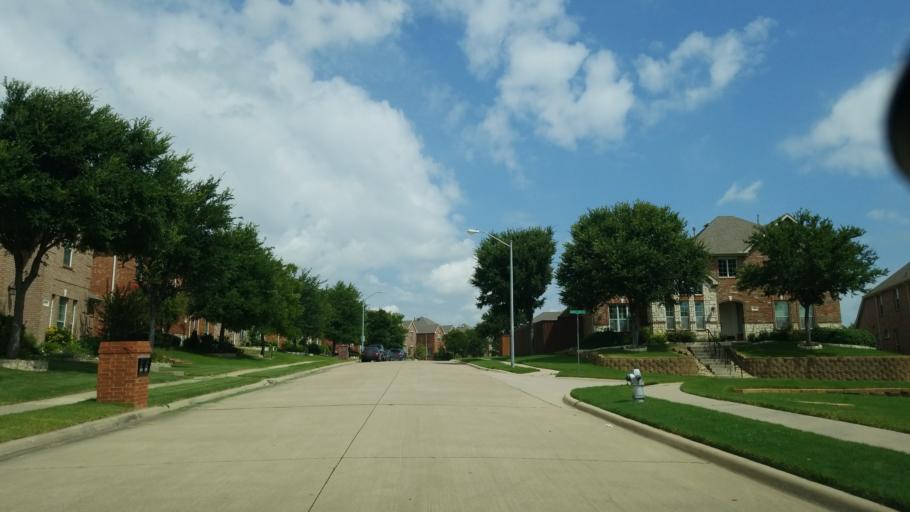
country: US
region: Texas
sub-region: Dallas County
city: Coppell
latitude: 32.9290
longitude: -96.9624
